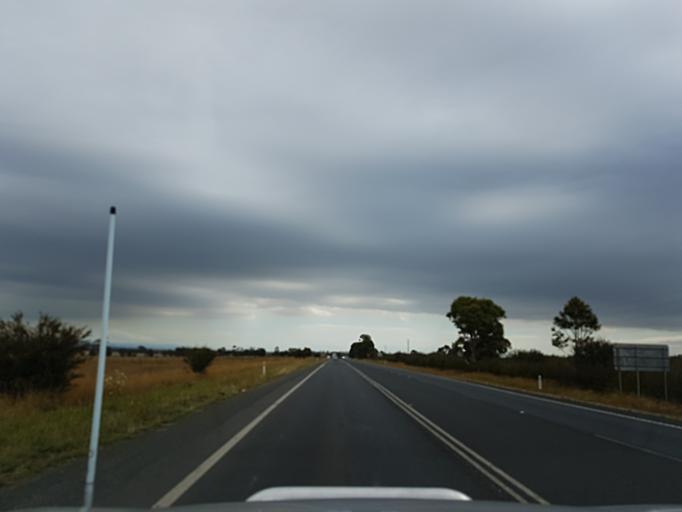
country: AU
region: Victoria
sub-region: Wellington
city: Heyfield
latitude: -38.1267
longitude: 146.8376
